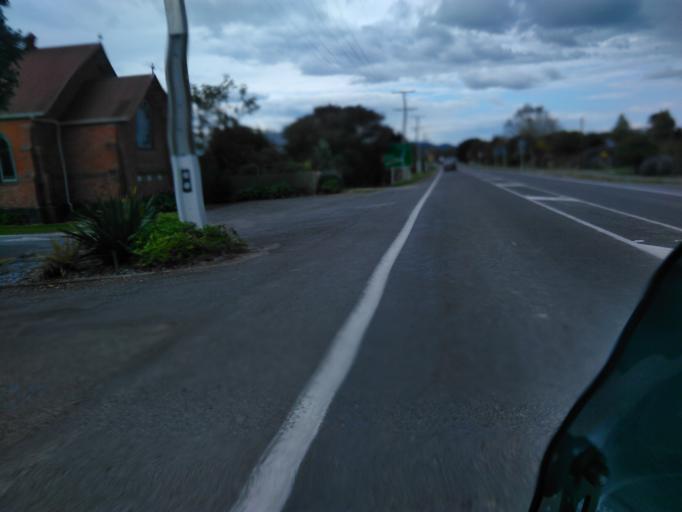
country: NZ
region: Gisborne
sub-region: Gisborne District
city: Gisborne
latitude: -38.6515
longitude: 177.9606
